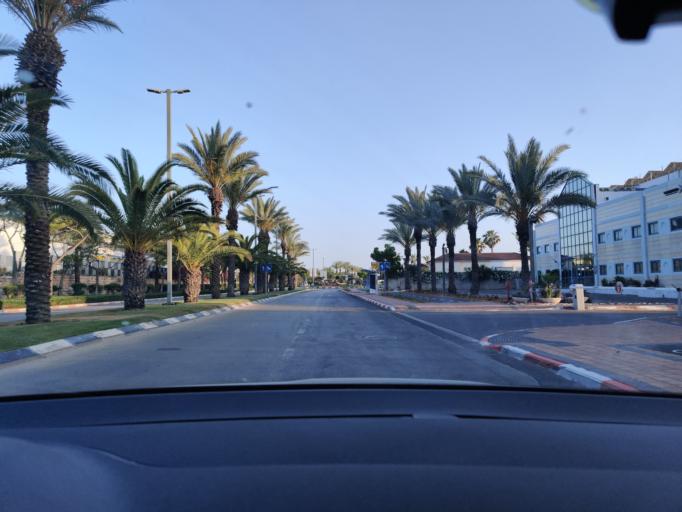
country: IL
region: Haifa
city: Qesarya
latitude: 32.4828
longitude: 34.9481
